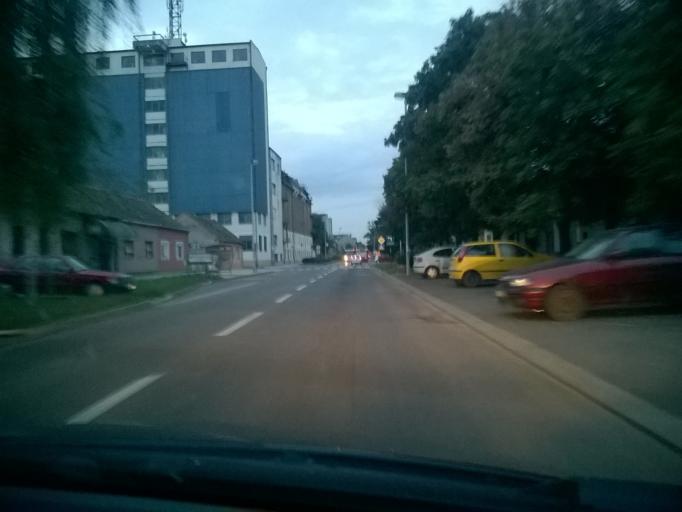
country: RS
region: Autonomna Pokrajina Vojvodina
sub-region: Juznobanatski Okrug
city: Pancevo
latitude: 44.8606
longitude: 20.6494
